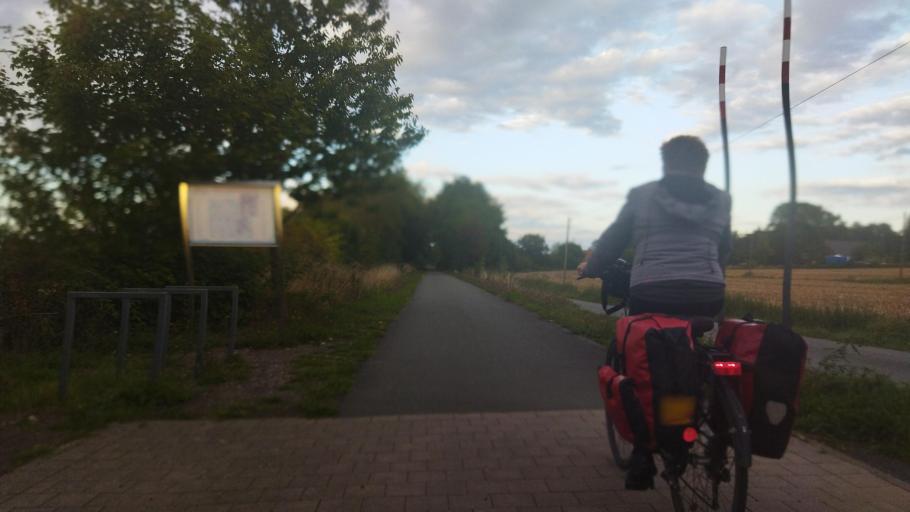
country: DE
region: North Rhine-Westphalia
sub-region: Regierungsbezirk Munster
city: Billerbeck
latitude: 52.0118
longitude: 7.2650
